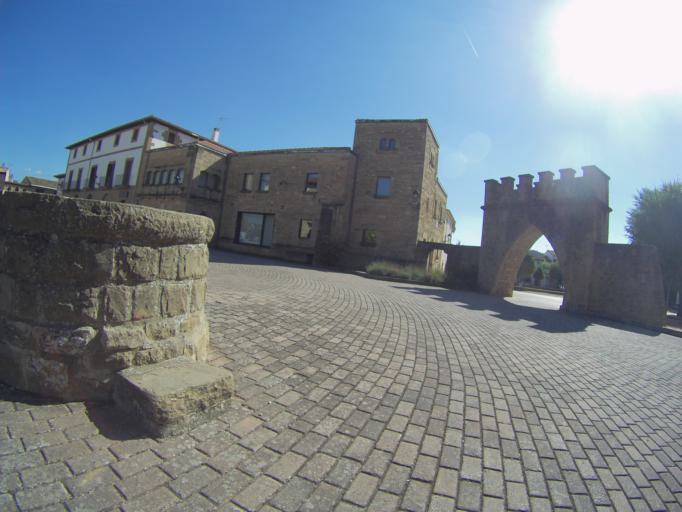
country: ES
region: Navarre
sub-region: Provincia de Navarra
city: Obanos
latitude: 42.6795
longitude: -1.7862
